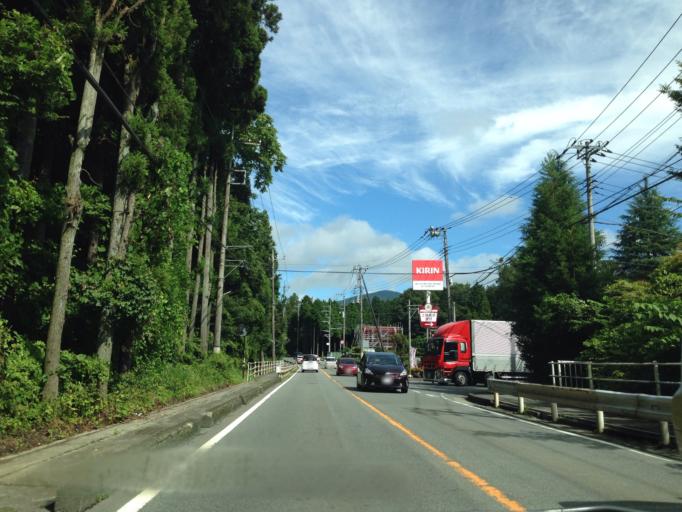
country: JP
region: Shizuoka
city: Gotemba
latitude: 35.3348
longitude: 138.8962
